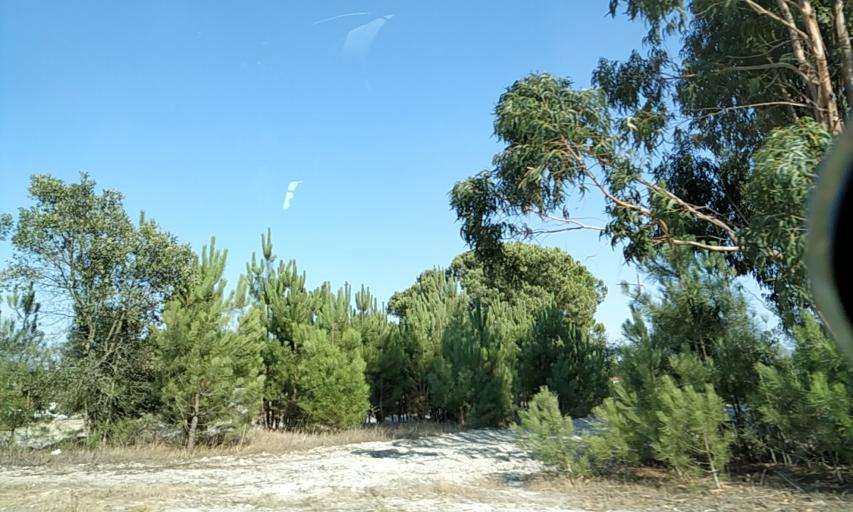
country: PT
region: Santarem
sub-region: Coruche
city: Coruche
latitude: 38.8304
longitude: -8.5621
